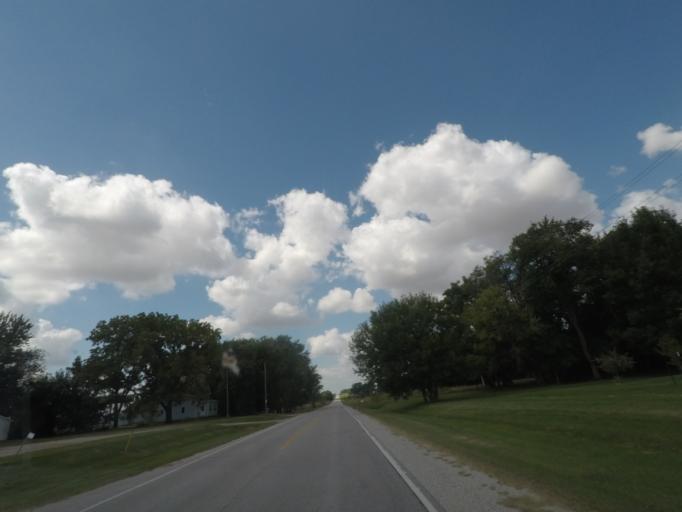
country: US
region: Iowa
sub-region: Story County
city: Nevada
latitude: 42.0226
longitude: -93.3330
